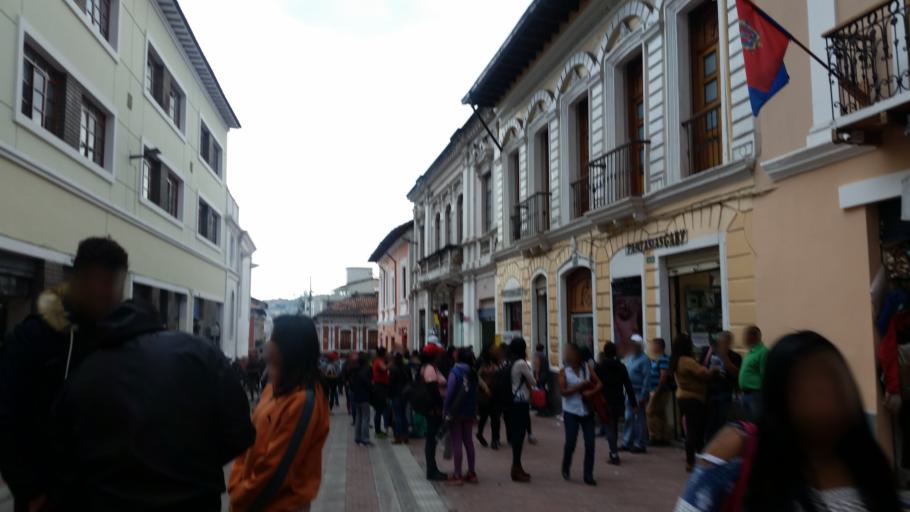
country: EC
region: Pichincha
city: Quito
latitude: -0.2180
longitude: -78.5144
